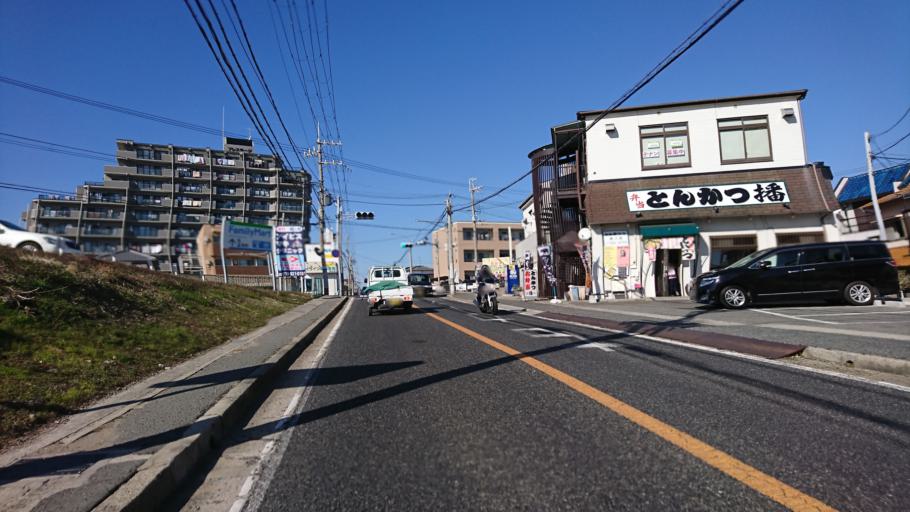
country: JP
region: Hyogo
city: Akashi
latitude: 34.6616
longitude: 134.9496
